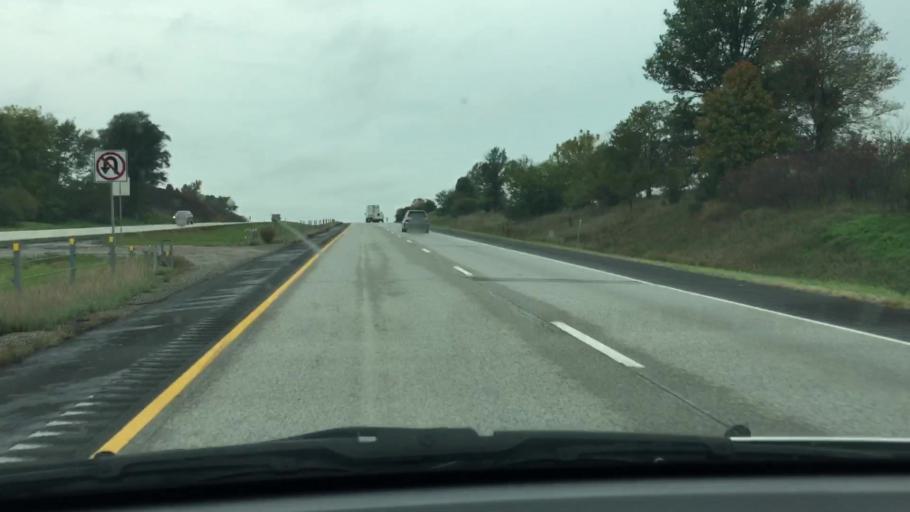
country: US
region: Iowa
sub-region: Johnson County
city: Tiffin
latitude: 41.6953
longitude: -91.7145
